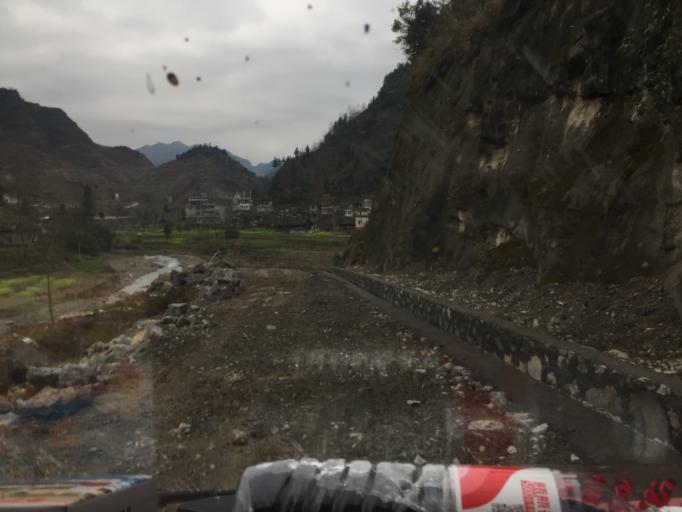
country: CN
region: Guizhou Sheng
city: Changfeng
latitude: 28.4306
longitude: 108.0790
